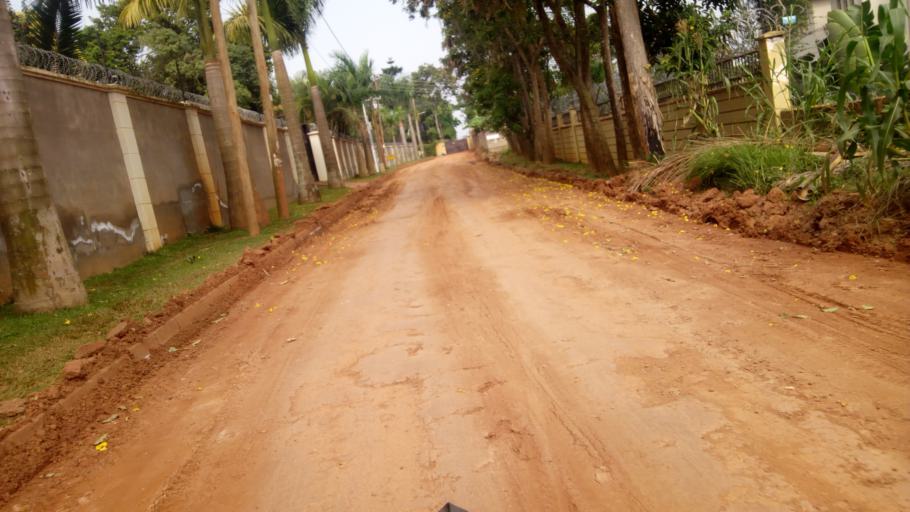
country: UG
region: Central Region
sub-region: Wakiso District
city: Kireka
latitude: 0.2906
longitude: 32.6600
